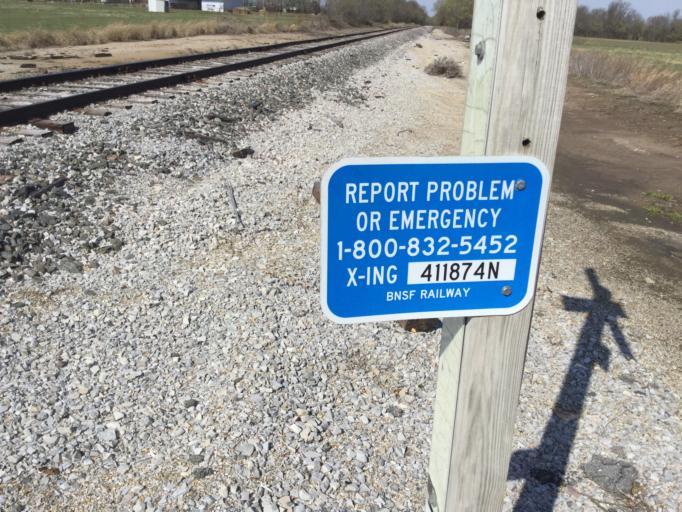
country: US
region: Kansas
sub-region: Cherokee County
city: Columbus
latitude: 37.1316
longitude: -94.7590
